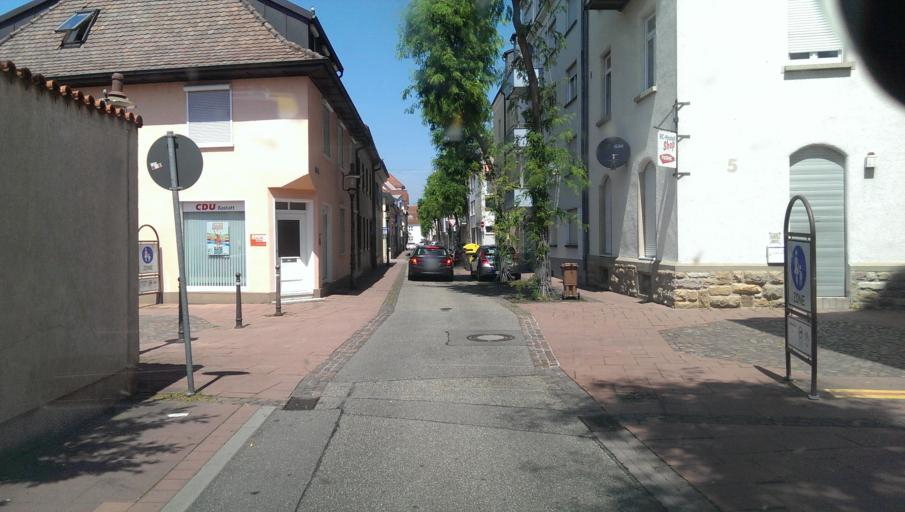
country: DE
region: Baden-Wuerttemberg
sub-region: Karlsruhe Region
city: Rastatt
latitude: 48.8579
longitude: 8.2012
